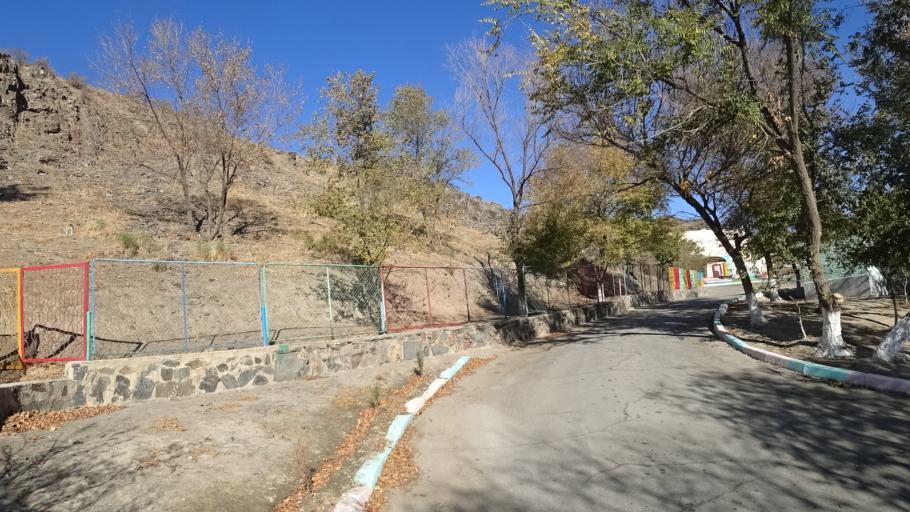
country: UZ
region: Navoiy
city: Karmana Shahri
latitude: 40.2918
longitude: 65.6012
